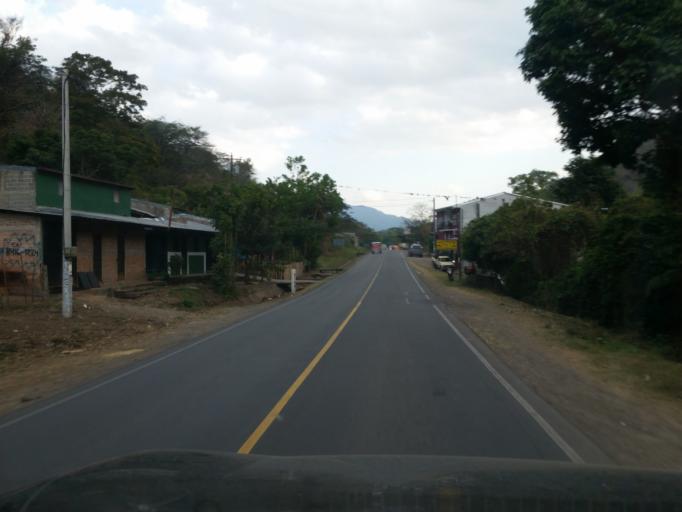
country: NI
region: Jinotega
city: Jinotega
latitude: 13.1130
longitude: -86.0061
